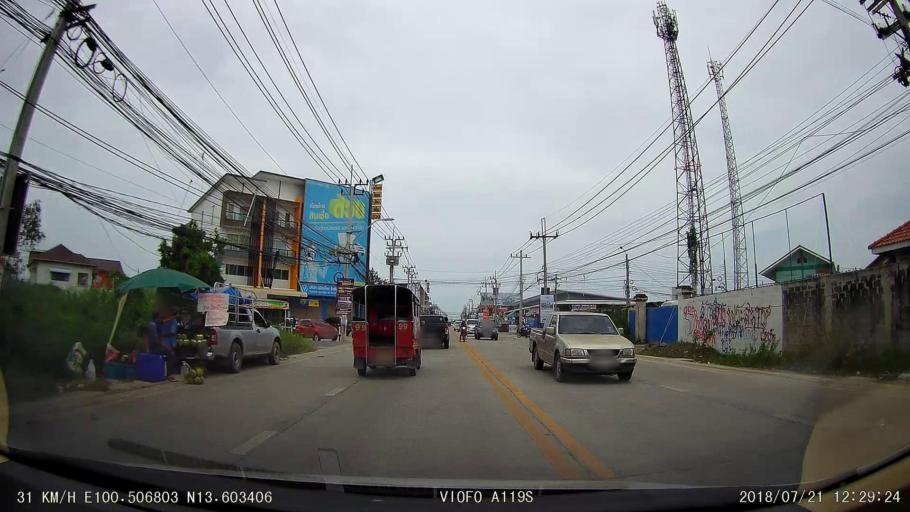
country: TH
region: Bangkok
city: Thung Khru
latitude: 13.6034
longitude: 100.5068
